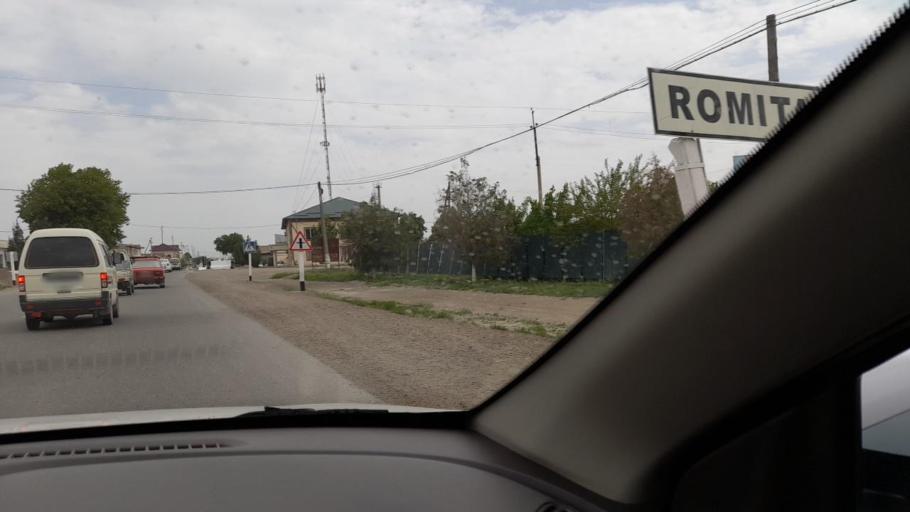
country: UZ
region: Bukhara
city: Romiton
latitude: 39.9387
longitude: 64.3639
